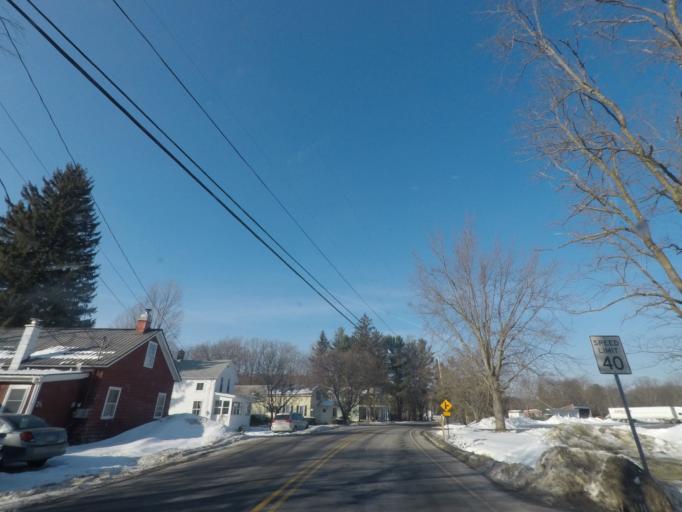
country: US
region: Massachusetts
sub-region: Berkshire County
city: Richmond
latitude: 42.4669
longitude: -73.3926
